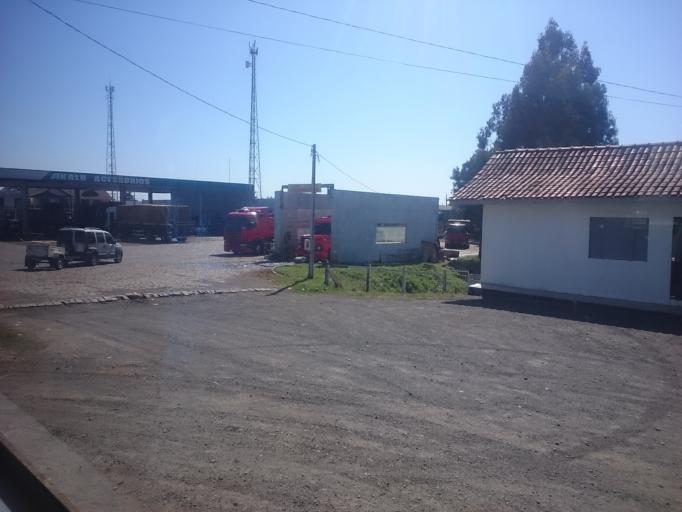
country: BR
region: Santa Catarina
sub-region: Santa Cecilia
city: Santa Cecilia
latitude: -26.9612
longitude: -50.4144
